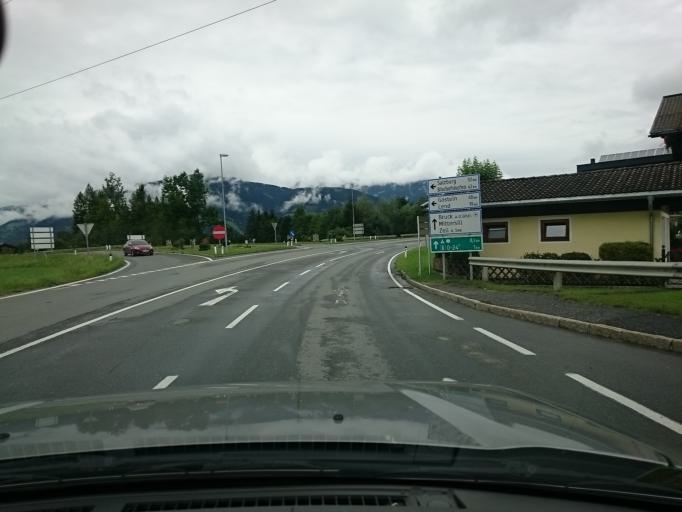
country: AT
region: Salzburg
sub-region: Politischer Bezirk Zell am See
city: Bruck an der Grossglocknerstrasse
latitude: 47.2788
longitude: 12.8256
